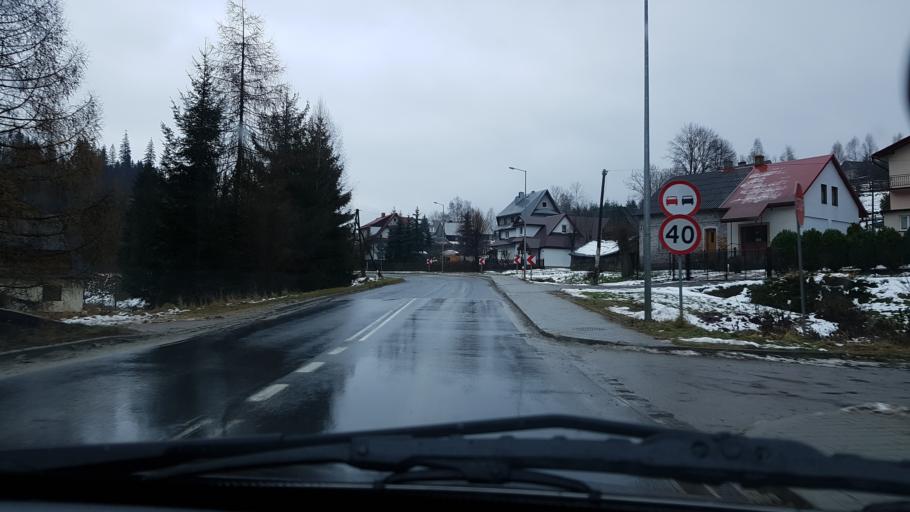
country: PL
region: Lesser Poland Voivodeship
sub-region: Powiat nowotarski
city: Raba Wyzna
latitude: 49.5445
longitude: 19.8903
